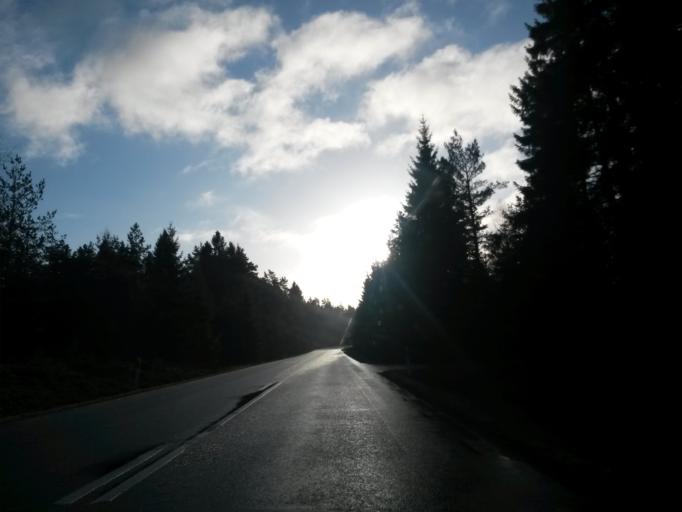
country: SE
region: Vaestra Goetaland
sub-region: Vargarda Kommun
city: Vargarda
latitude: 57.9822
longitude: 12.8133
